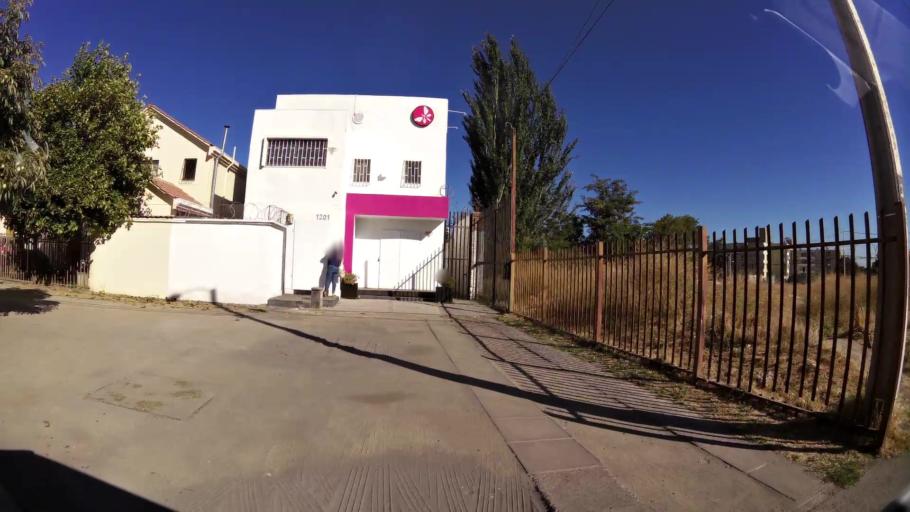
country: CL
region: O'Higgins
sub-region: Provincia de Cachapoal
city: Rancagua
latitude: -34.1866
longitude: -70.7274
